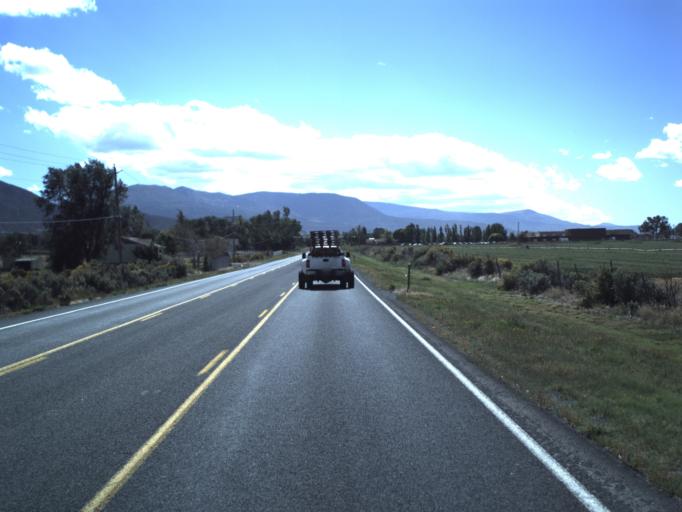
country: US
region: Utah
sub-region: Iron County
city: Enoch
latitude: 37.7536
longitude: -113.0553
